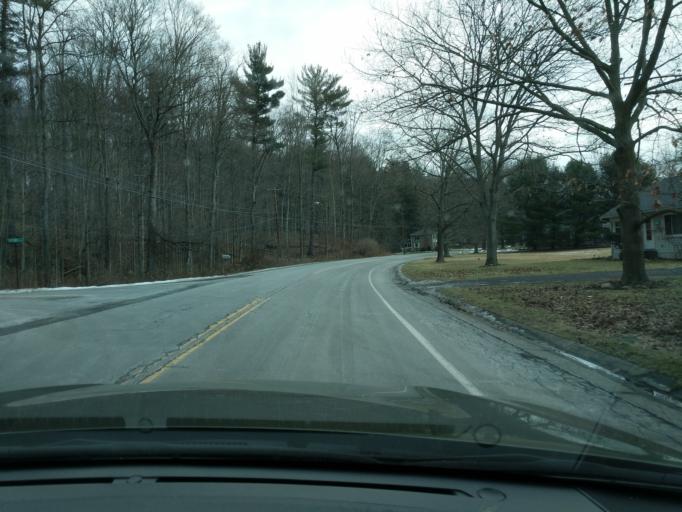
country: US
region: New York
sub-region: Tompkins County
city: East Ithaca
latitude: 42.3887
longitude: -76.4086
